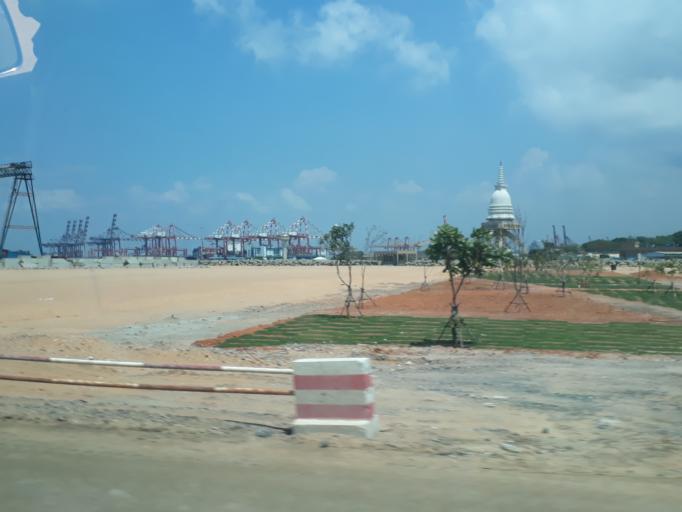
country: LK
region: Western
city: Colombo
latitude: 6.9365
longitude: 79.8375
